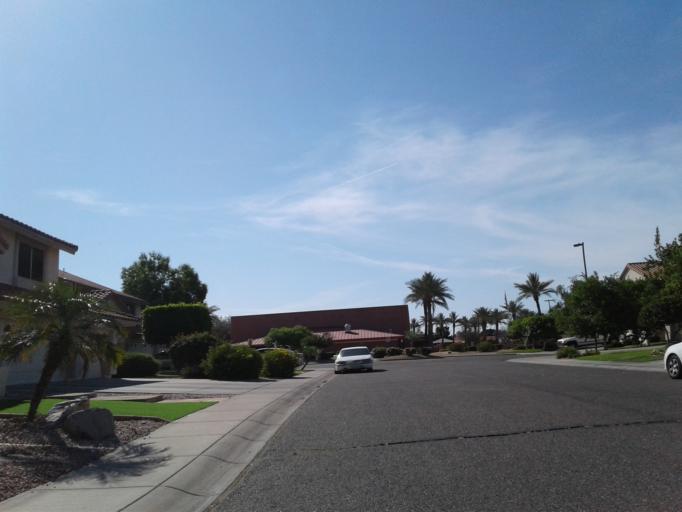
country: US
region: Arizona
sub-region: Maricopa County
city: Peoria
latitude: 33.6007
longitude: -112.1809
